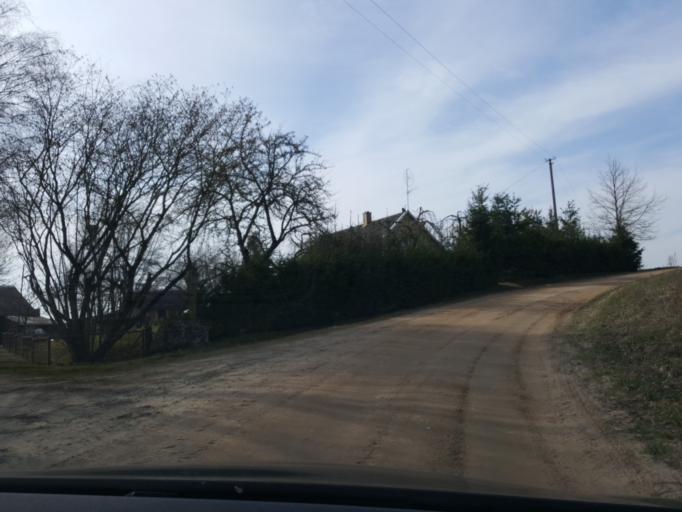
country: LT
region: Alytaus apskritis
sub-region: Alytus
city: Alytus
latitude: 54.3302
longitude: 23.8856
